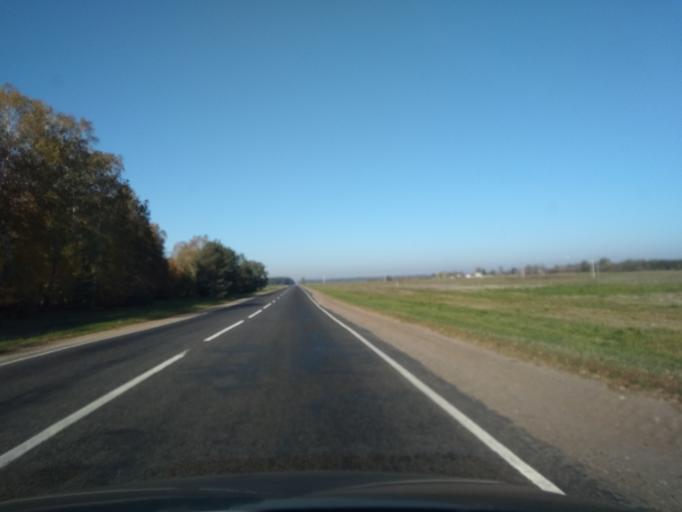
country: BY
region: Brest
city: Malaryta
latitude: 51.9361
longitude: 24.0465
